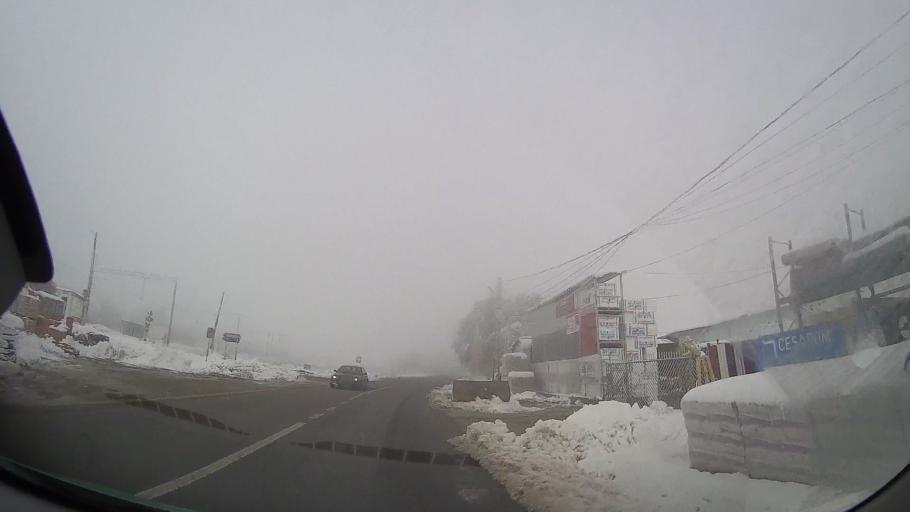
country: RO
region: Iasi
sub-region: Comuna Mircesti
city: Mircesti
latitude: 47.0904
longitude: 26.8226
